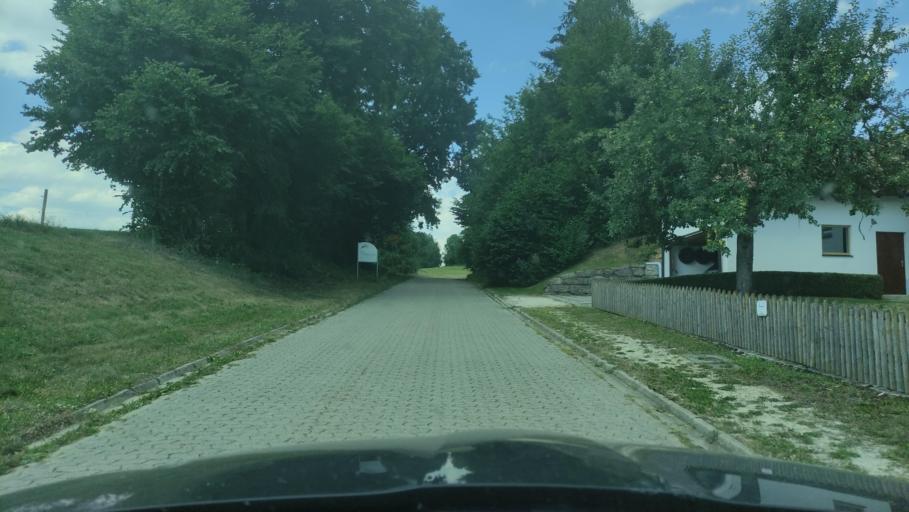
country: DE
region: Bavaria
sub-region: Swabia
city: Roggenburg
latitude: 48.2723
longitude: 10.2480
